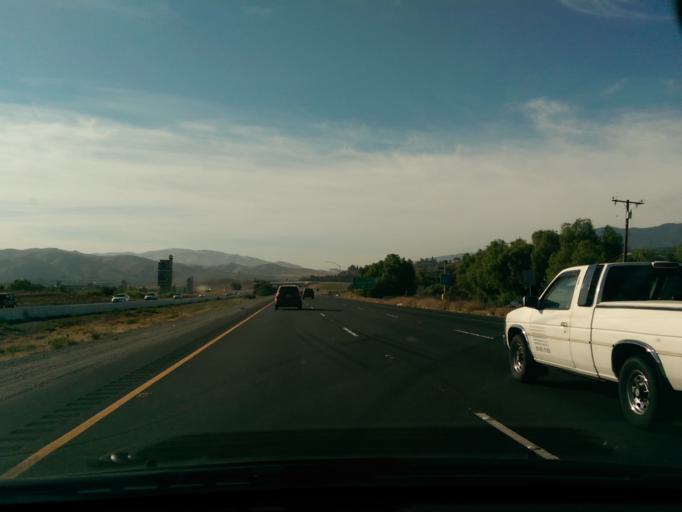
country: US
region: California
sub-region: Riverside County
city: El Cerrito
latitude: 33.8266
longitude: -117.5252
